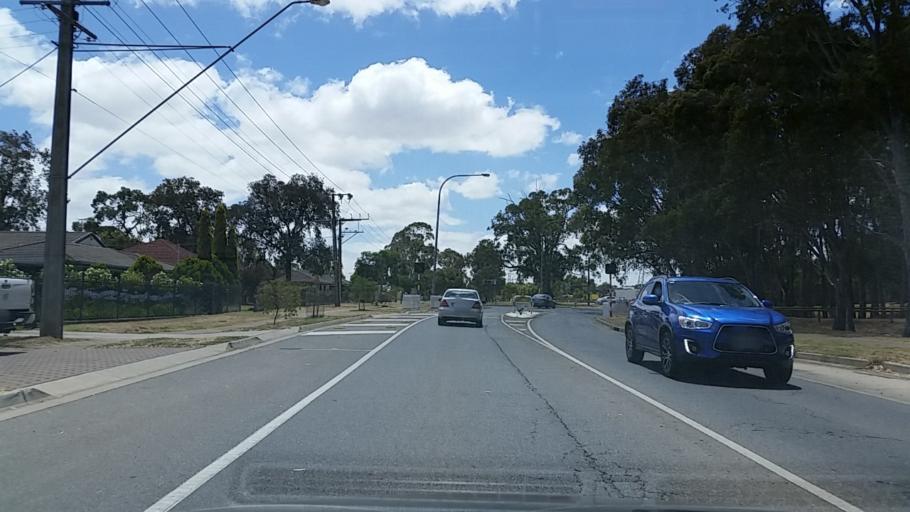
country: AU
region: South Australia
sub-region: Salisbury
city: Salisbury
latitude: -34.7692
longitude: 138.6194
